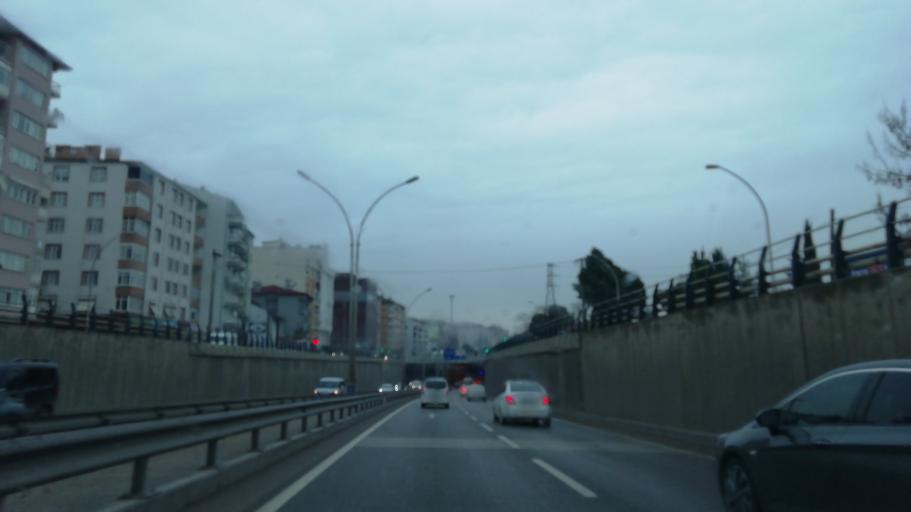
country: TR
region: Kocaeli
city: Izmit
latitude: 40.7663
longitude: 29.9073
